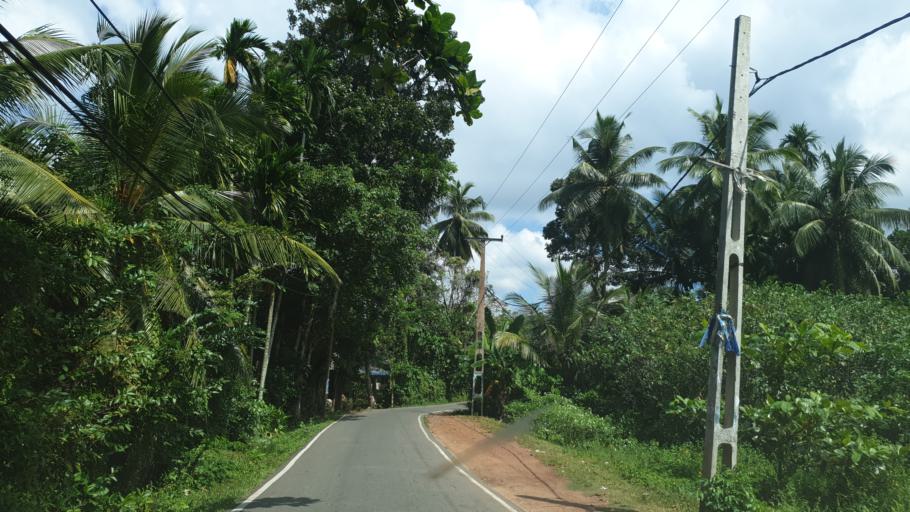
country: LK
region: Western
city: Panadura
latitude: 6.6794
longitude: 79.9399
